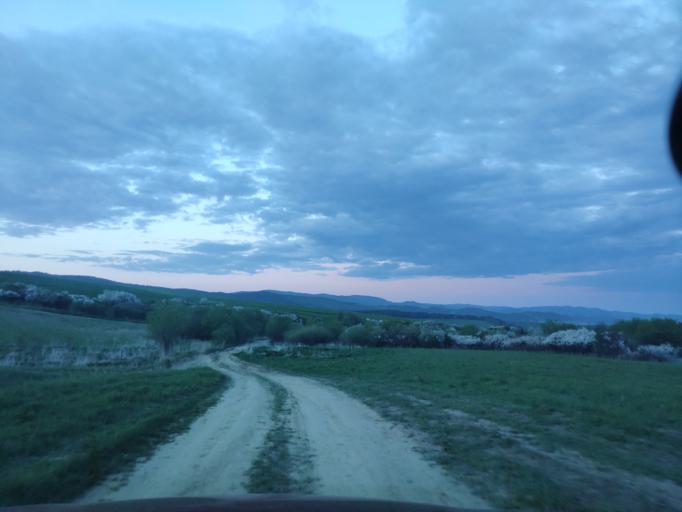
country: SK
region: Presovsky
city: Lipany
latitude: 49.1803
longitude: 20.8226
